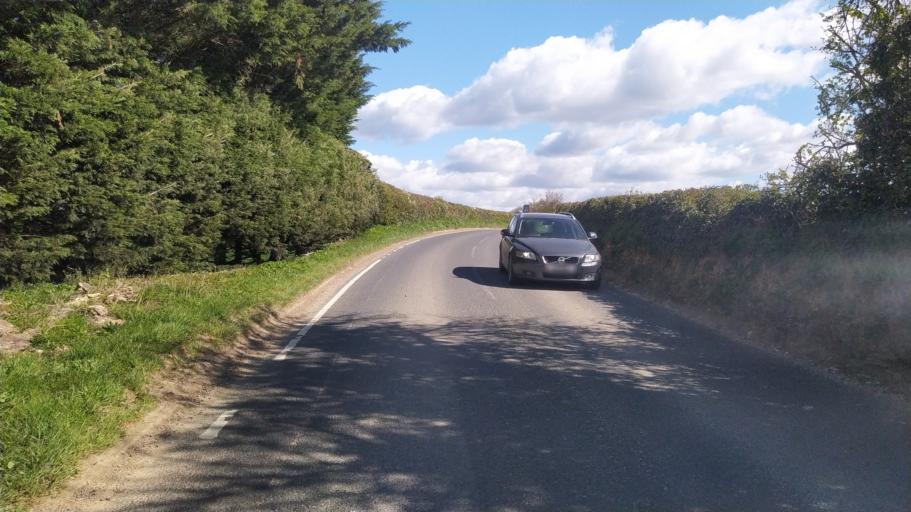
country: GB
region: England
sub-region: Dorset
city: Manston
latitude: 50.9764
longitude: -2.2926
